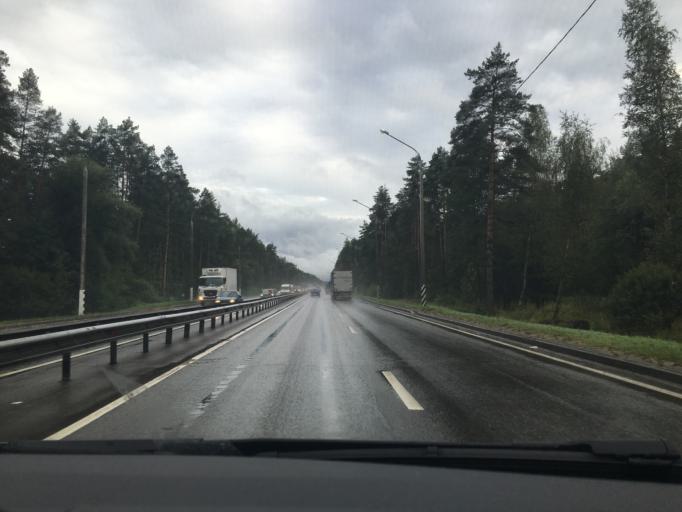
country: RU
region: Kaluga
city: Obninsk
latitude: 55.0648
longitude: 36.6226
